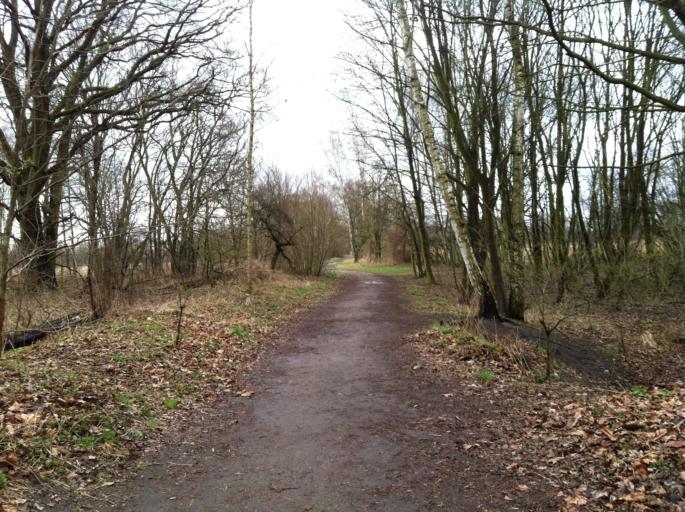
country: DE
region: Berlin
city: Karow
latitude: 52.6227
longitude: 13.4594
